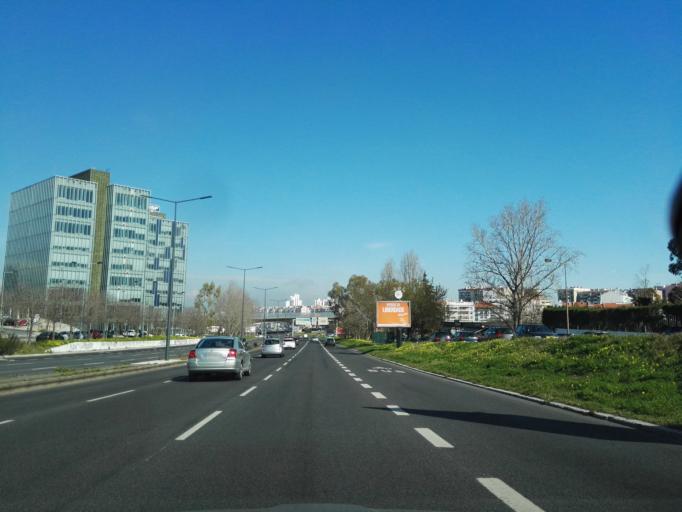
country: PT
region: Lisbon
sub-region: Odivelas
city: Olival do Basto
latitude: 38.7684
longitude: -9.1648
